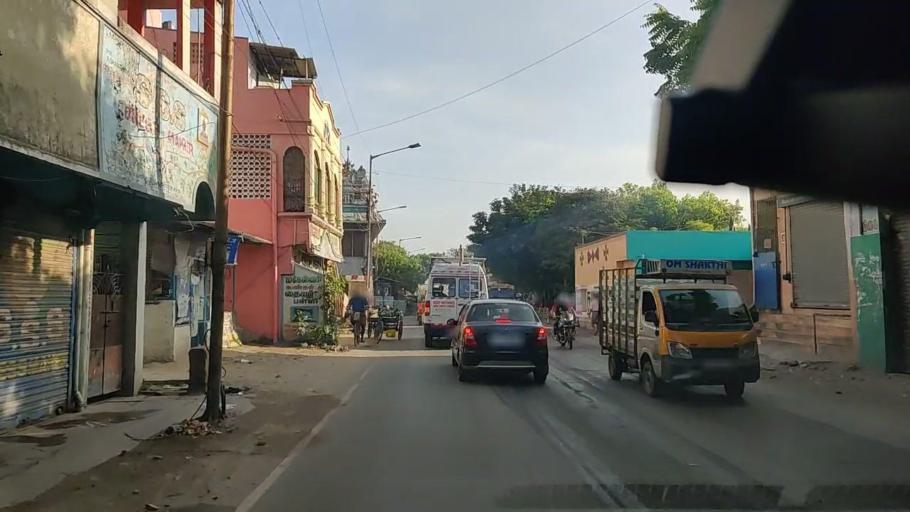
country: IN
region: Tamil Nadu
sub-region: Chennai
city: George Town
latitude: 13.1154
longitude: 80.2617
